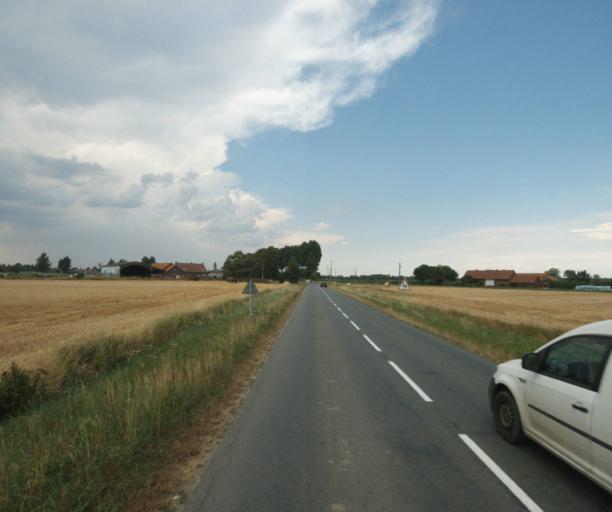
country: FR
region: Nord-Pas-de-Calais
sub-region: Departement du Nord
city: Deulemont
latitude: 50.7413
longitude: 2.9551
